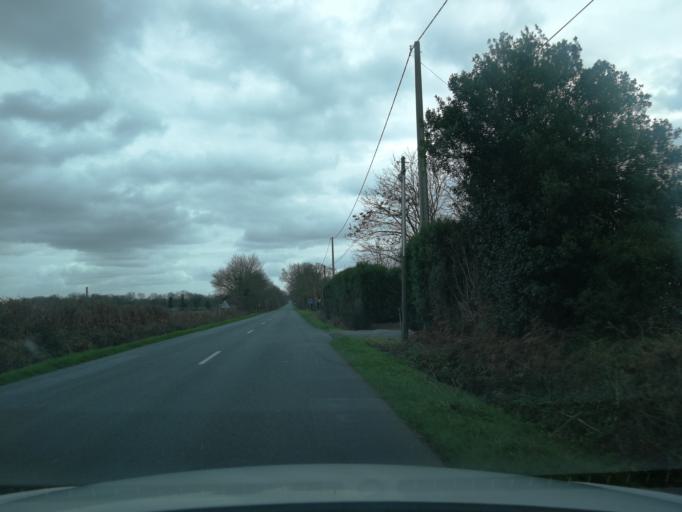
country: FR
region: Pays de la Loire
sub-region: Departement de la Loire-Atlantique
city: Montbert
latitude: 47.0227
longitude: -1.4913
